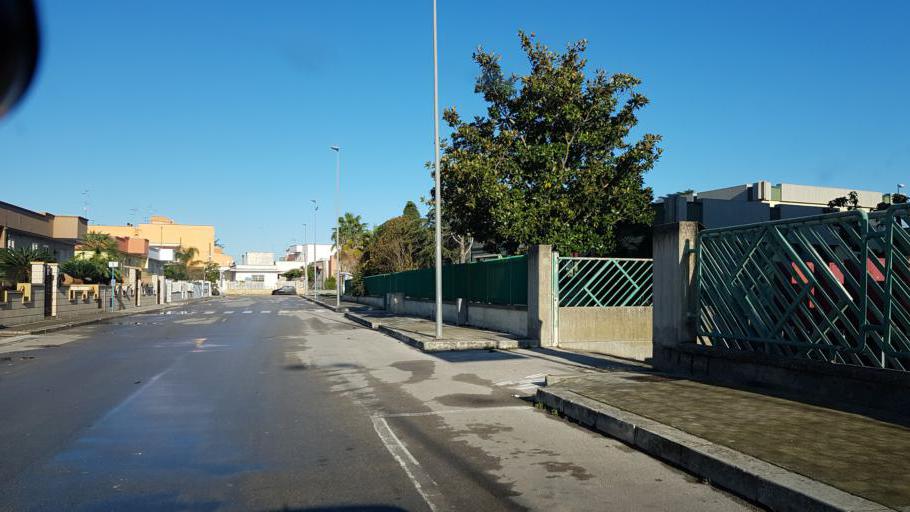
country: IT
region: Apulia
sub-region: Provincia di Brindisi
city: Torchiarolo
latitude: 40.4801
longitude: 18.0555
